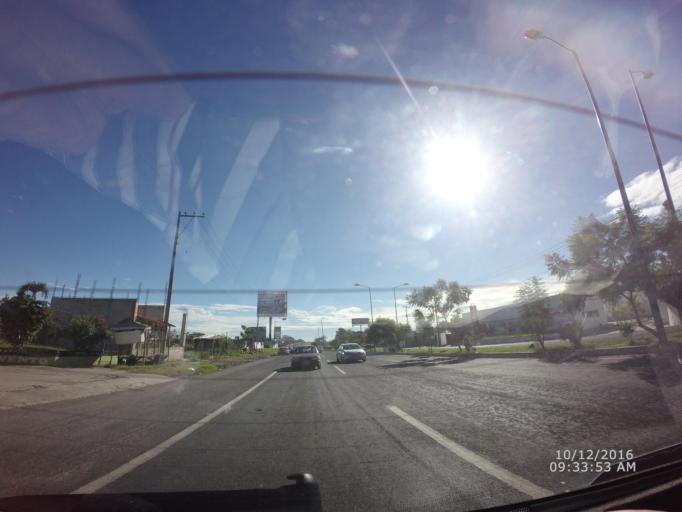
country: MX
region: Veracruz
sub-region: Emiliano Zapata
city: Las Trancas
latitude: 19.5076
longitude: -96.8622
